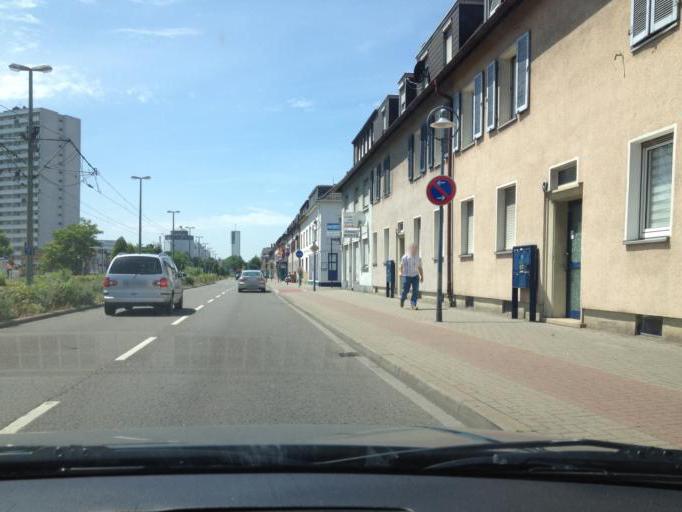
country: DE
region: Rheinland-Pfalz
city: Ludwigshafen am Rhein
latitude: 49.4682
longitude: 8.4347
